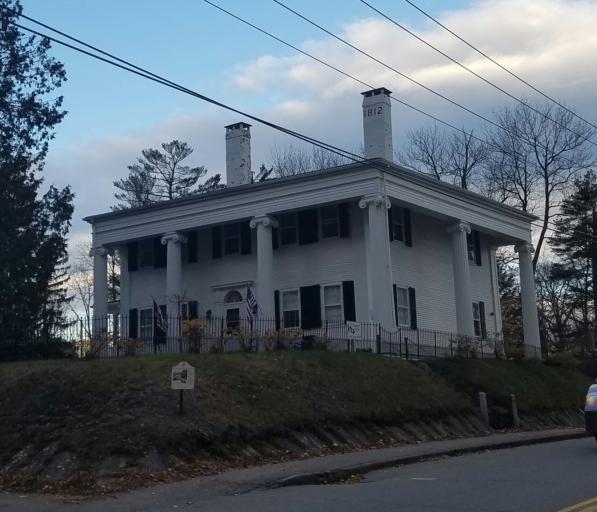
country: US
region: Maine
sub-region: Waldo County
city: Belfast
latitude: 44.4274
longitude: -69.0103
